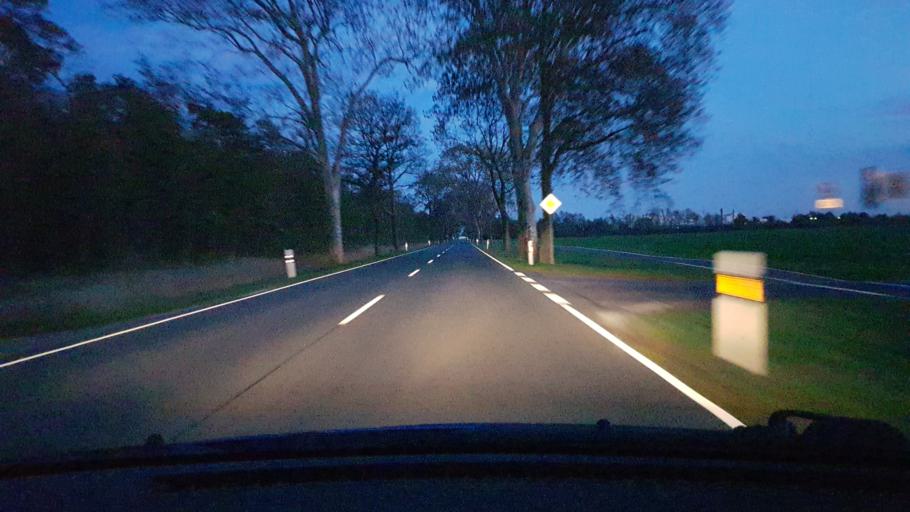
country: DE
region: Saxony-Anhalt
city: Rodleben
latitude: 51.9067
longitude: 12.2034
